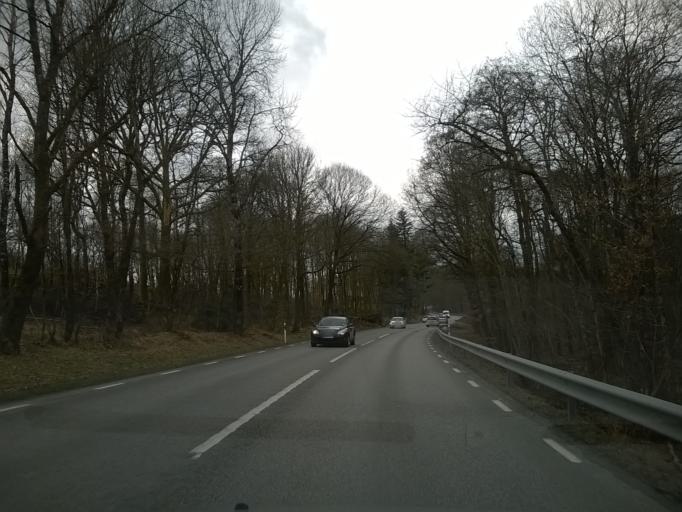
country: SE
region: Halland
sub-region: Varbergs Kommun
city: Tvaaker
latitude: 57.1450
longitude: 12.4947
